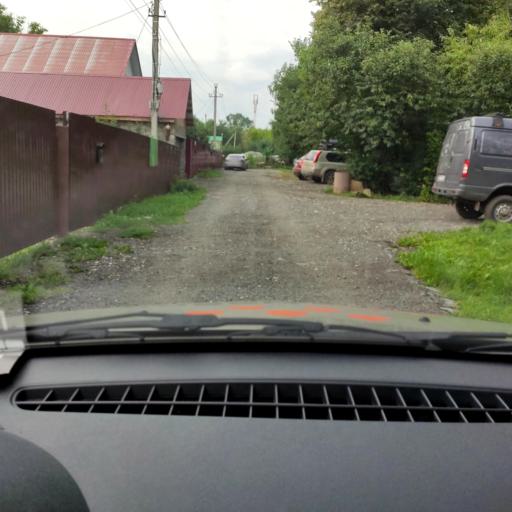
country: RU
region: Bashkortostan
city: Mikhaylovka
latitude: 54.7947
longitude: 55.9381
